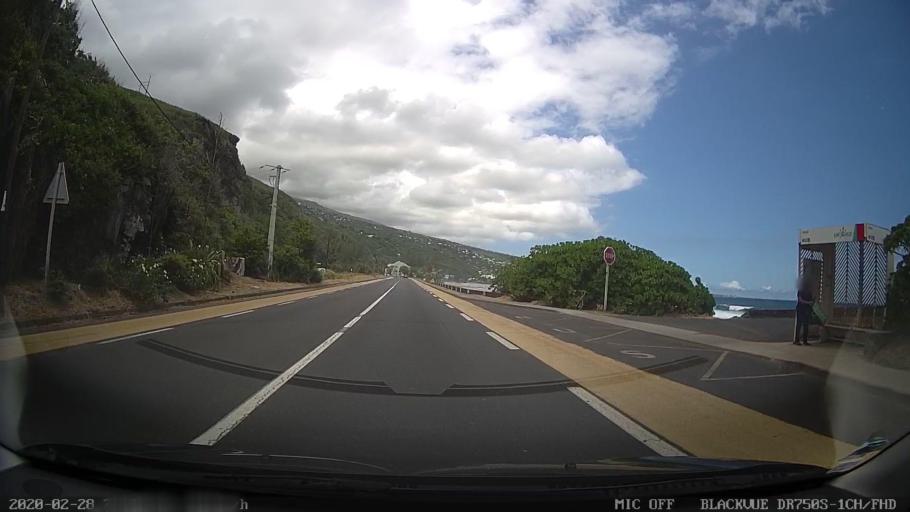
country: RE
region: Reunion
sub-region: Reunion
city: Saint-Leu
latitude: -21.1560
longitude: 55.2834
